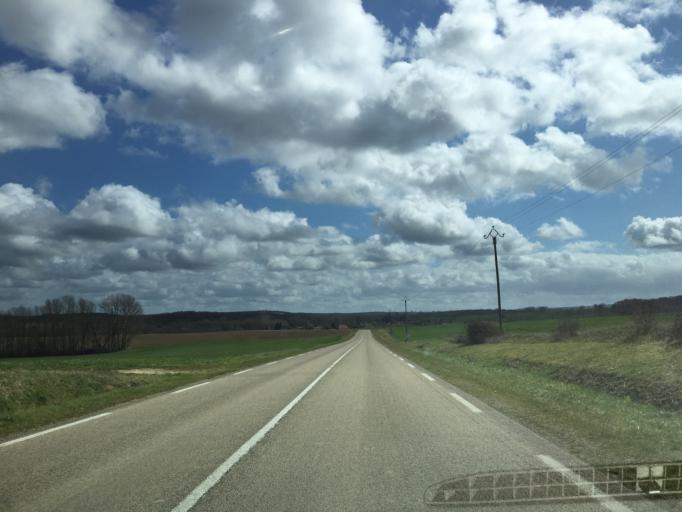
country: FR
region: Bourgogne
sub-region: Departement de l'Yonne
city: Aillant-sur-Tholon
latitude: 47.8494
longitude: 3.3819
